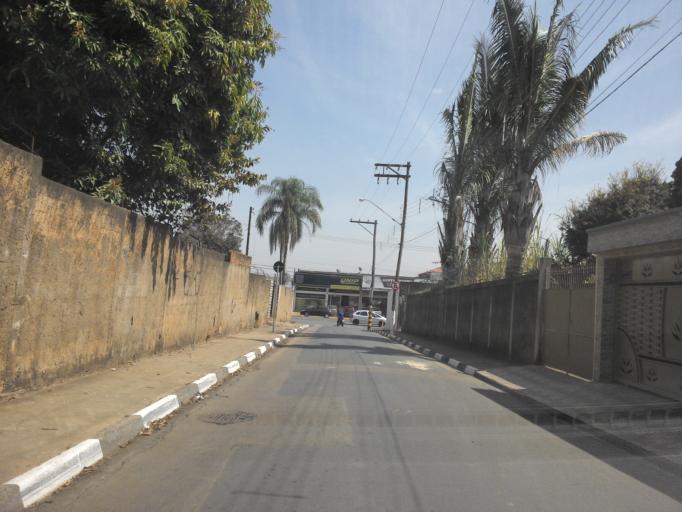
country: BR
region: Sao Paulo
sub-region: Hortolandia
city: Hortolandia
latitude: -22.8975
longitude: -47.2294
